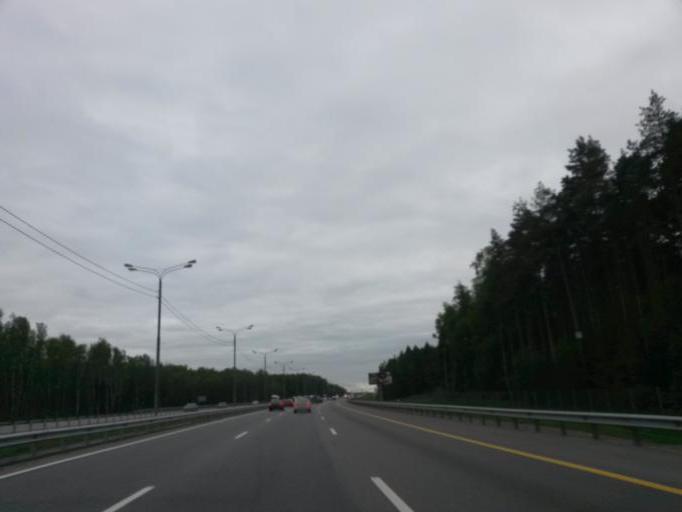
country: RU
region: Moskovskaya
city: Vostryakovo
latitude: 55.4391
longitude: 37.7988
